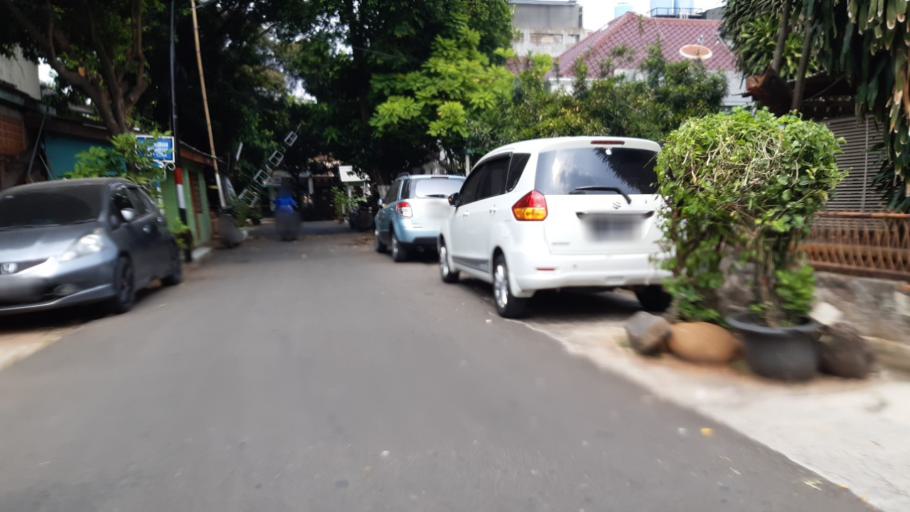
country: ID
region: Jakarta Raya
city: Jakarta
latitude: -6.2333
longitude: 106.8544
